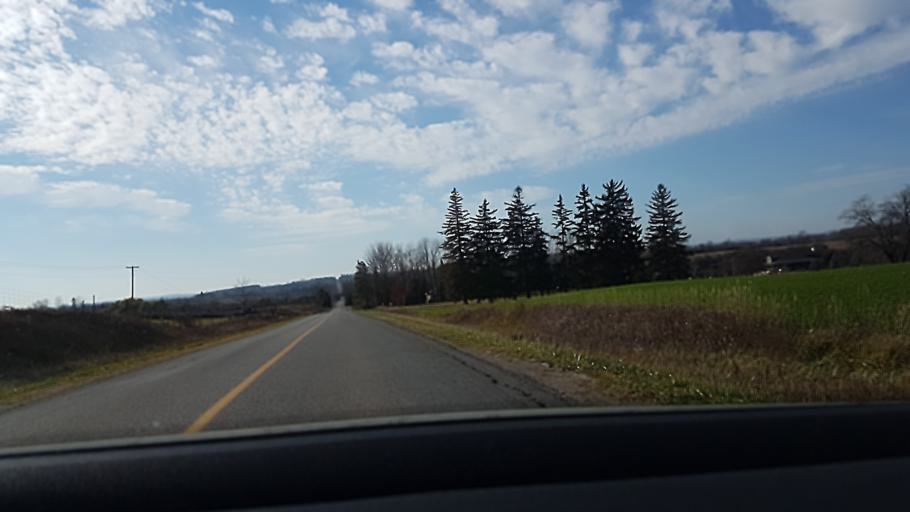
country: CA
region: Ontario
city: Bradford West Gwillimbury
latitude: 44.0632
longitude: -79.7954
